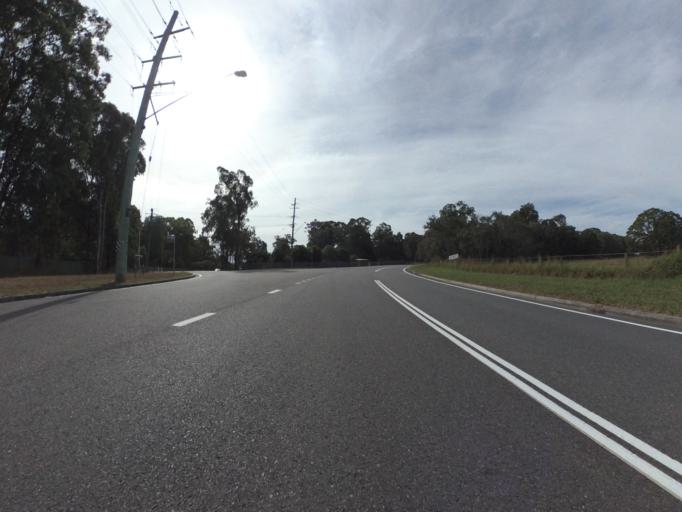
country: AU
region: Queensland
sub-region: Brisbane
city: Moggill
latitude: -27.5771
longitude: 152.8630
